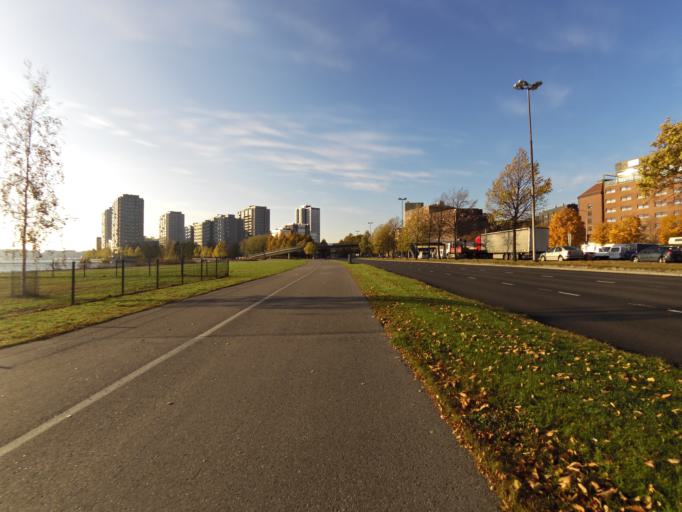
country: FI
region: Uusimaa
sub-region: Helsinki
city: Helsinki
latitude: 60.1830
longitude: 24.9636
